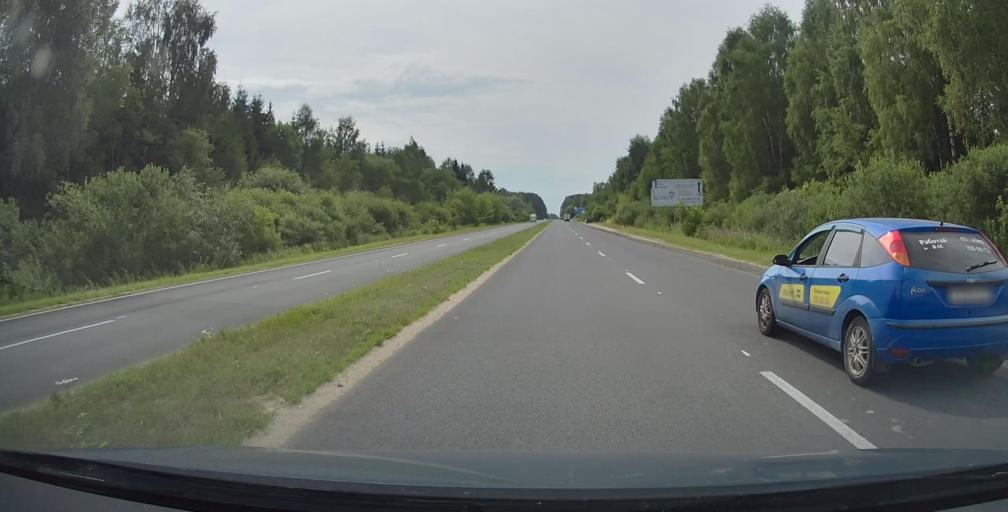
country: RU
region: Jaroslavl
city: Rybinsk
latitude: 58.0213
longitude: 38.9711
